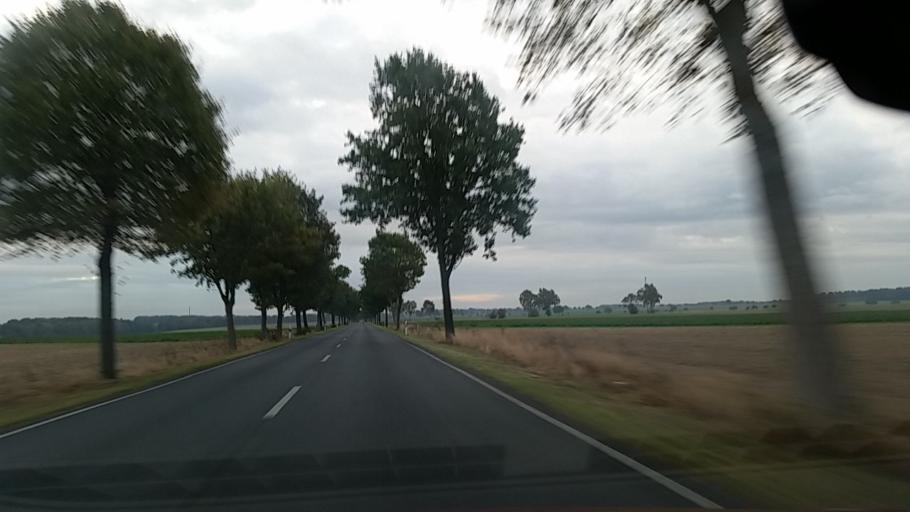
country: DE
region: Lower Saxony
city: Hankensbuttel
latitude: 52.7395
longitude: 10.5720
